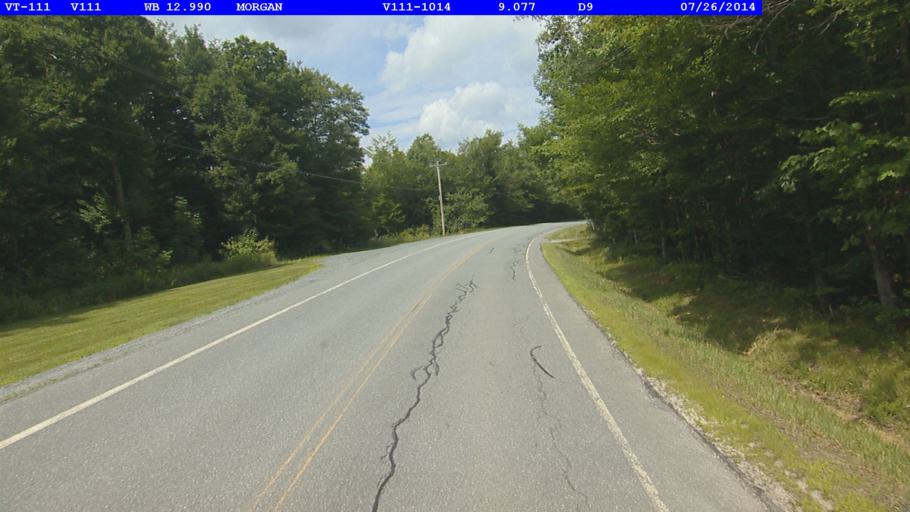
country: US
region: Vermont
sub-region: Orleans County
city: Newport
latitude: 44.8605
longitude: -71.9415
